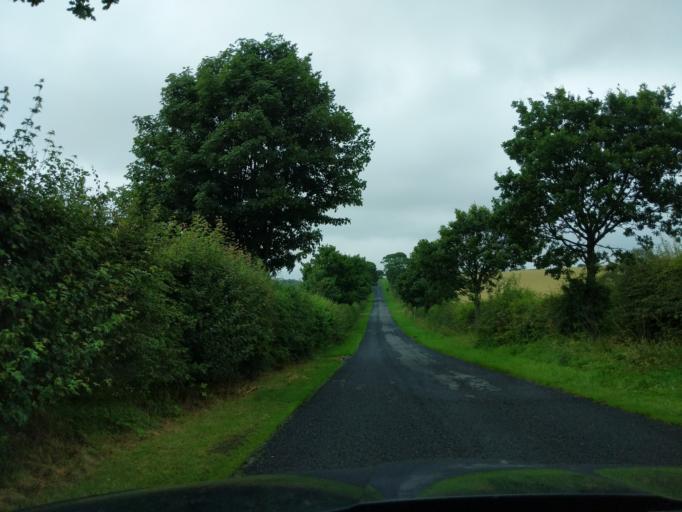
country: GB
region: England
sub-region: Northumberland
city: Ford
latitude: 55.6974
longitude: -2.1418
